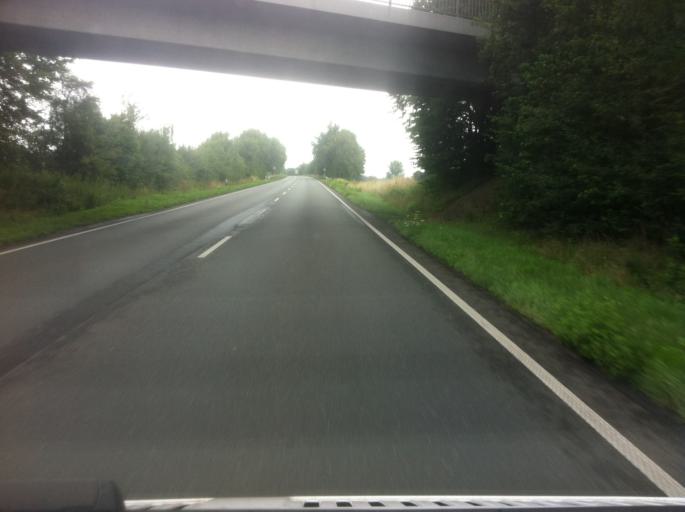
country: DE
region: North Rhine-Westphalia
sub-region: Regierungsbezirk Dusseldorf
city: Goch
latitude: 51.6827
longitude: 6.1270
